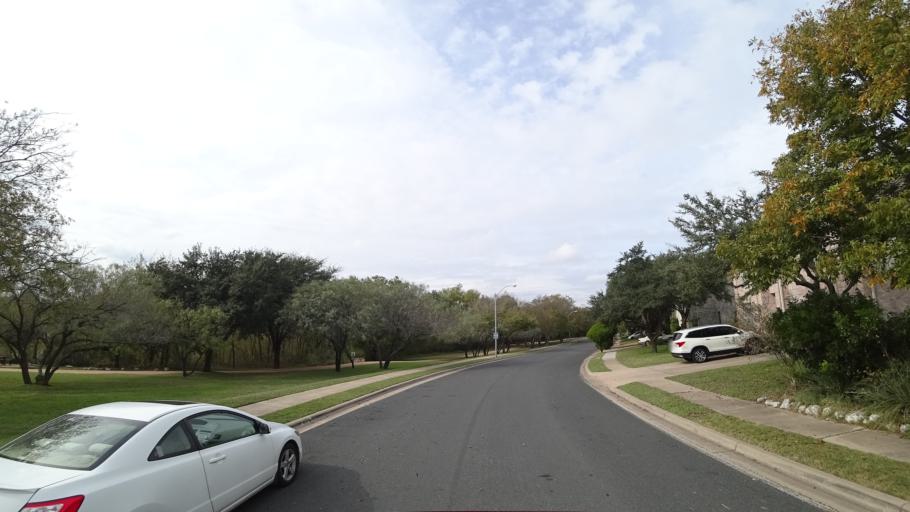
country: US
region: Texas
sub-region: Travis County
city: Wells Branch
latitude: 30.4510
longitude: -97.6791
